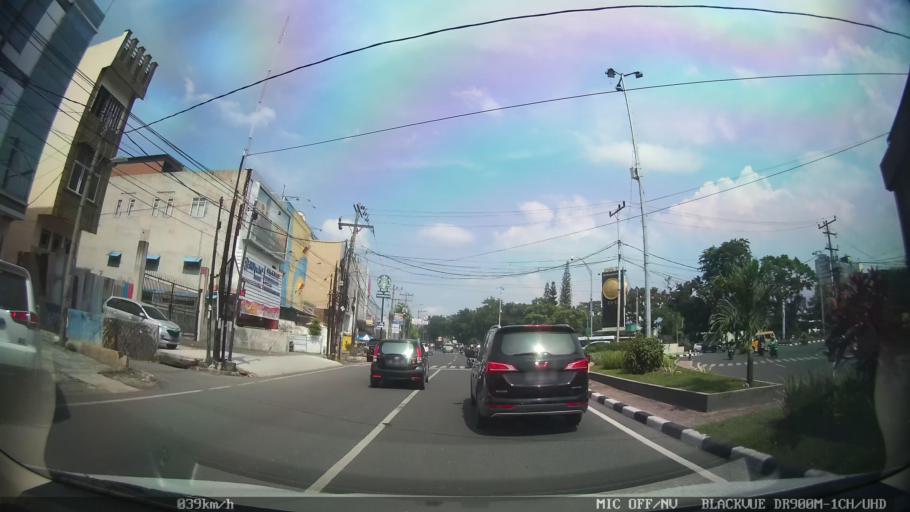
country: ID
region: North Sumatra
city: Medan
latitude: 3.6070
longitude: 98.6687
